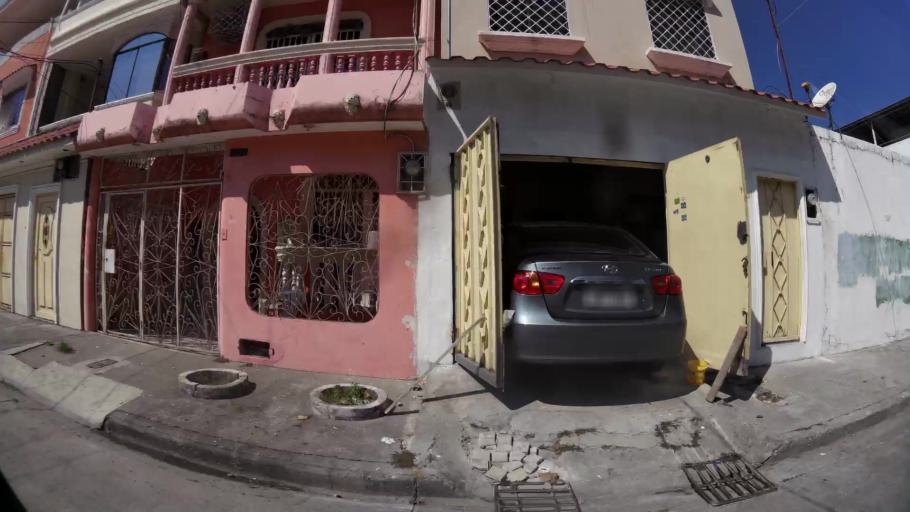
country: EC
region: Guayas
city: Guayaquil
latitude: -2.1882
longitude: -79.9160
